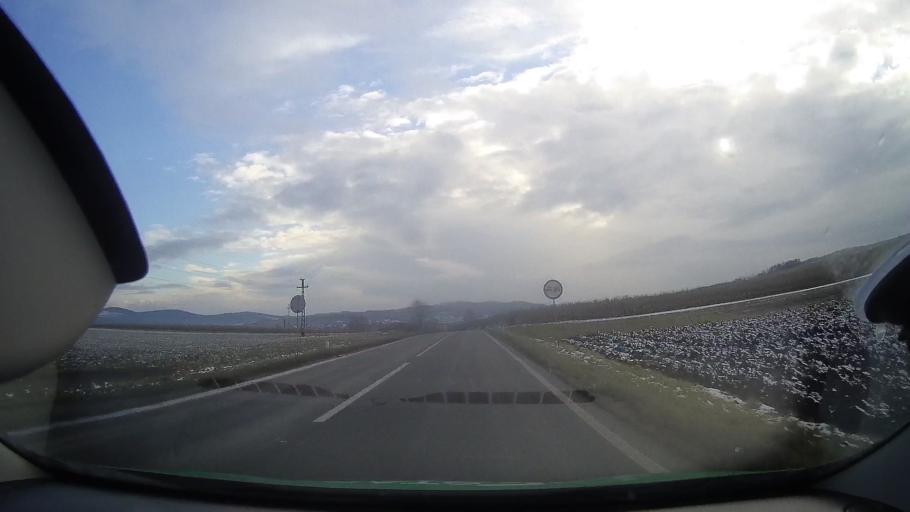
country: RO
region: Mures
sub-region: Comuna Cucerdea
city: Cucerdea
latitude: 46.4126
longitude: 24.2645
